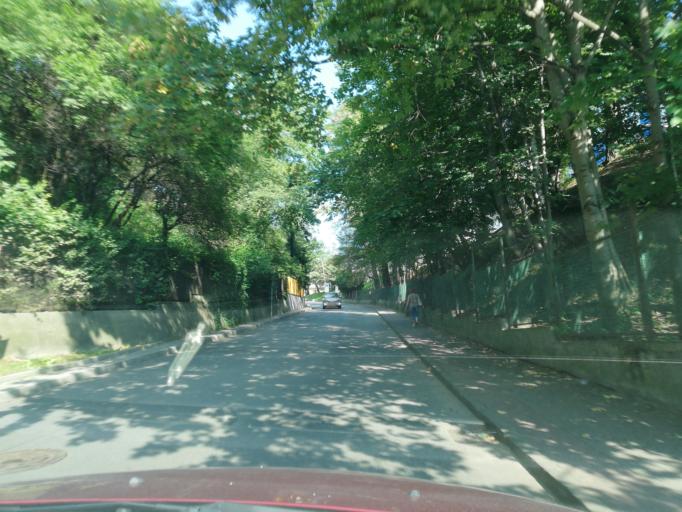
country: PL
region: Lesser Poland Voivodeship
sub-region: Powiat nowosadecki
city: Nowy Sacz
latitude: 49.6184
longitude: 20.6926
